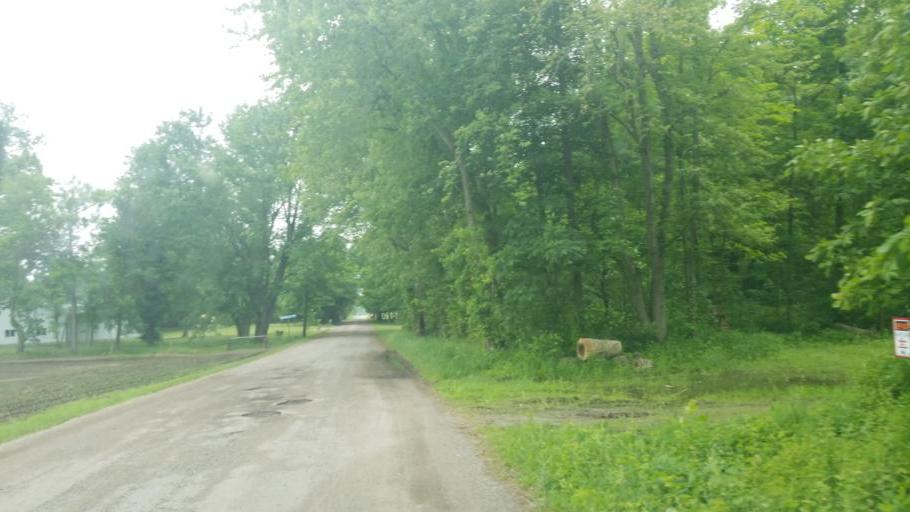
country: US
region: Indiana
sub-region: Elkhart County
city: Wakarusa
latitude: 41.4796
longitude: -86.0595
